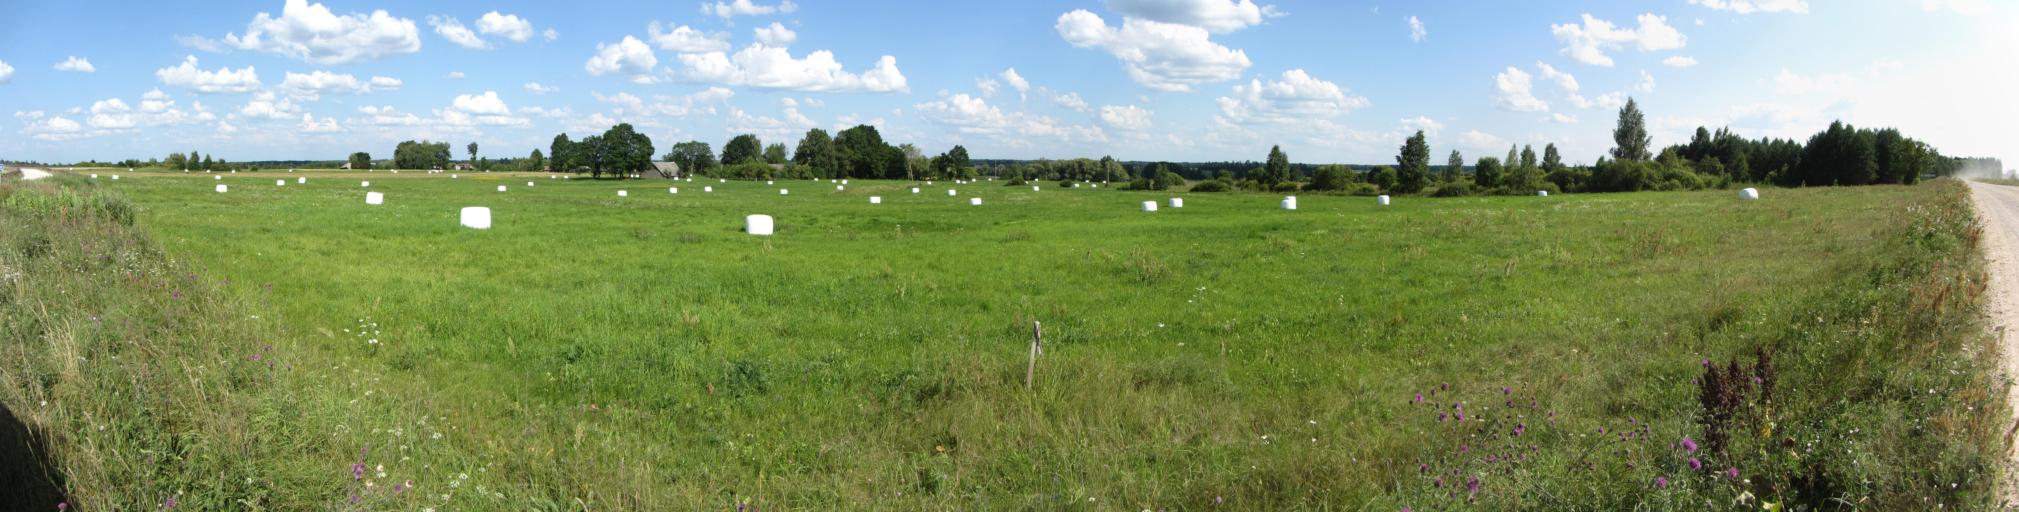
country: BY
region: Vitebsk
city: Vidzy
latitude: 55.2841
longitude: 26.5047
